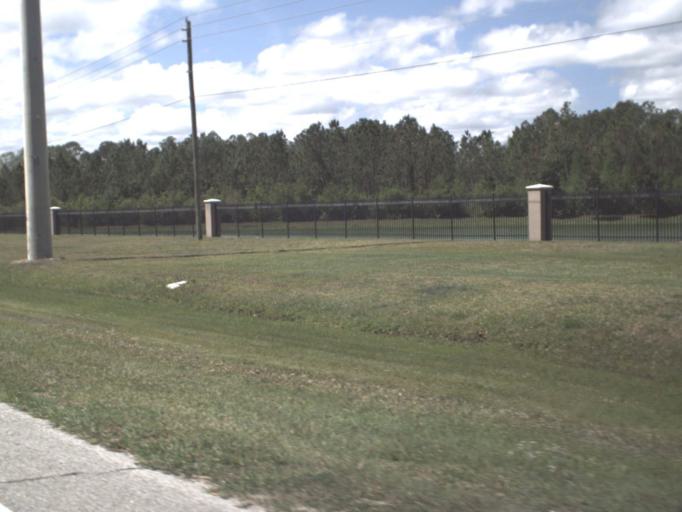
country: US
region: Florida
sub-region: Flagler County
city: Bunnell
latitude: 29.5051
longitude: -81.2646
